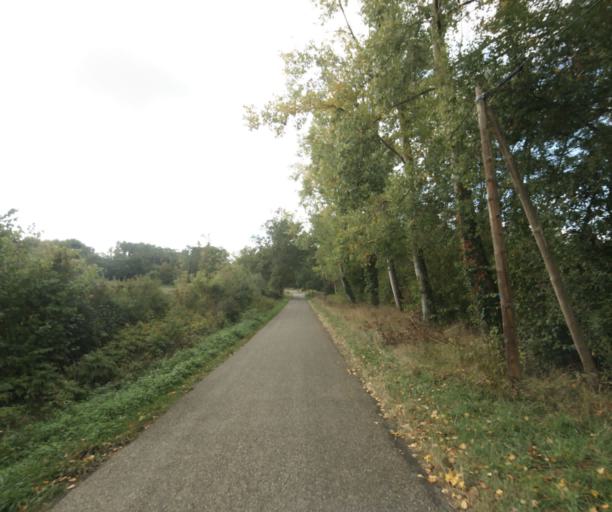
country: FR
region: Midi-Pyrenees
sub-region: Departement du Gers
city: Nogaro
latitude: 43.8263
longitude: -0.0861
